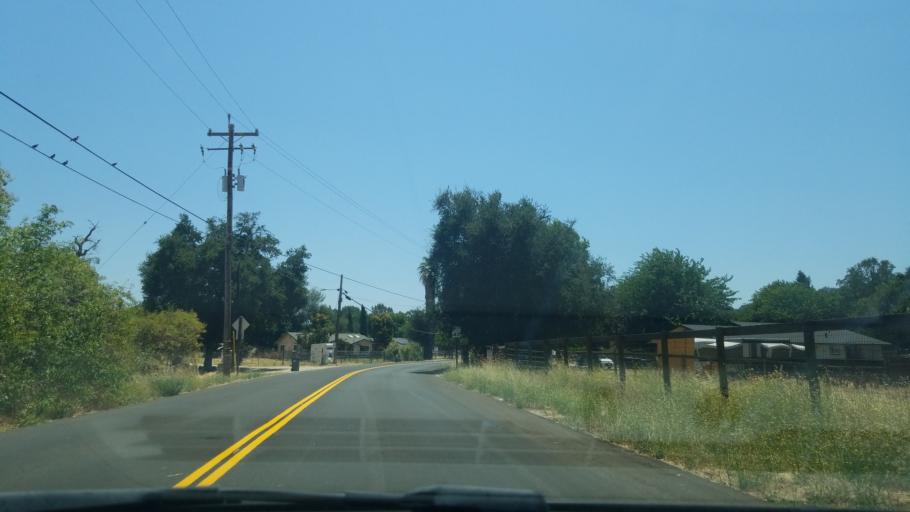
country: US
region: California
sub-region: San Luis Obispo County
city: Atascadero
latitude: 35.4922
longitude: -120.6470
